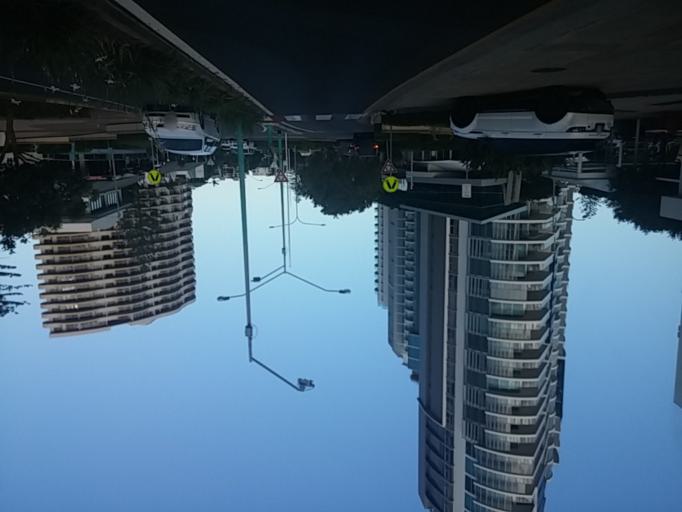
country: AU
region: New South Wales
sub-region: Tweed
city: Tweed Heads West
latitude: -28.1686
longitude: 153.5409
